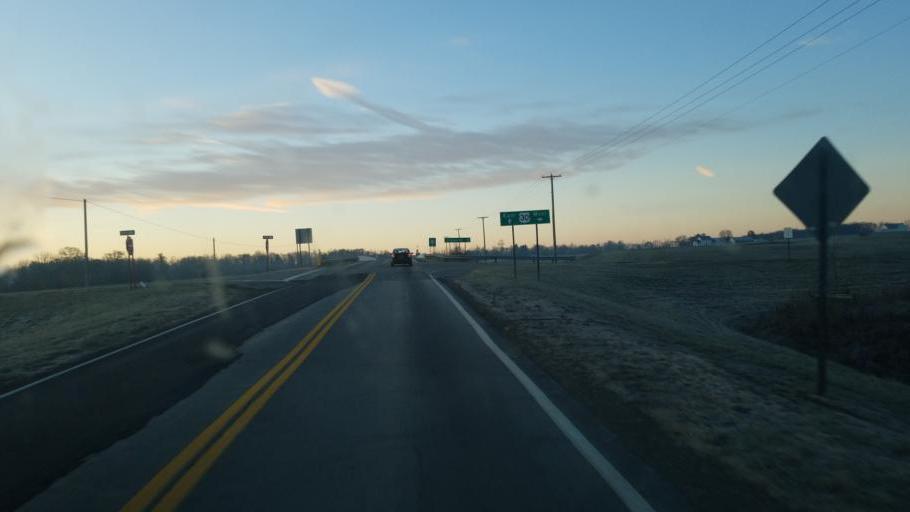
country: US
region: Ohio
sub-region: Wayne County
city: Orrville
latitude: 40.7952
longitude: -81.7851
